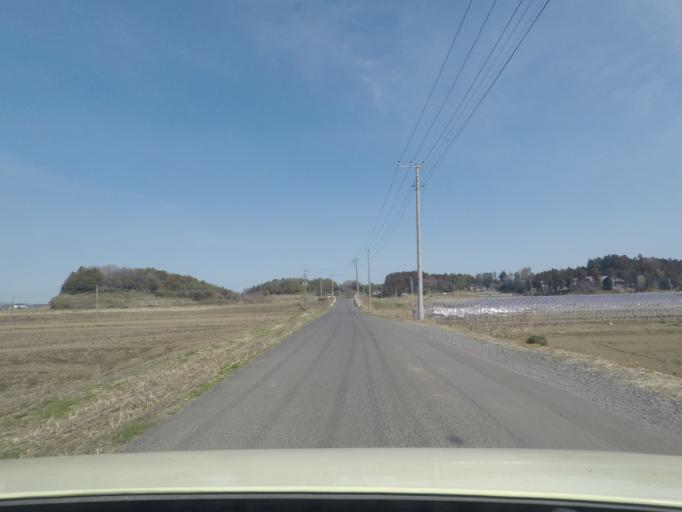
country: JP
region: Ibaraki
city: Ishioka
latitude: 36.1997
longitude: 140.3153
